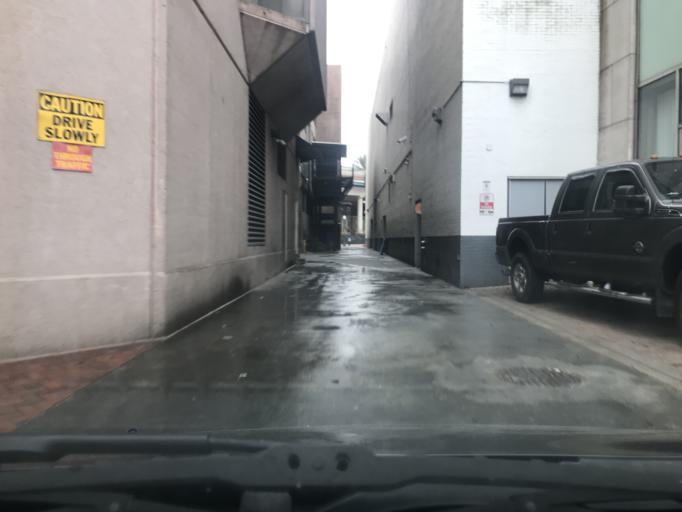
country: US
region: Louisiana
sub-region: Orleans Parish
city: New Orleans
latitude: 29.9492
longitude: -90.0668
